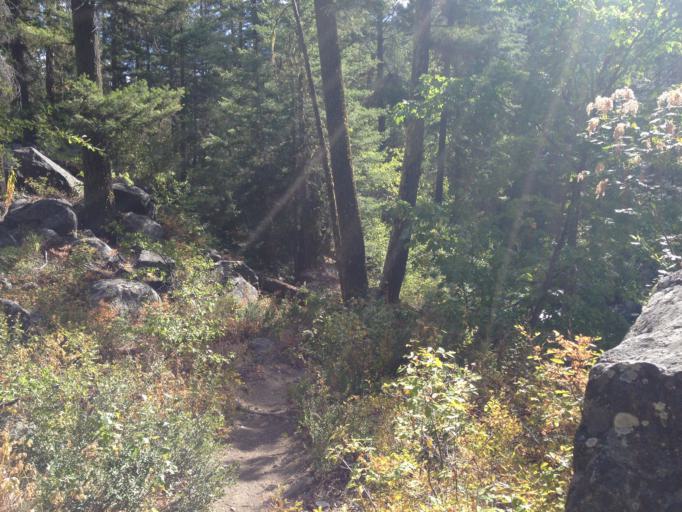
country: US
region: Washington
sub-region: Chelan County
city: Leavenworth
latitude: 47.4503
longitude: -120.7113
